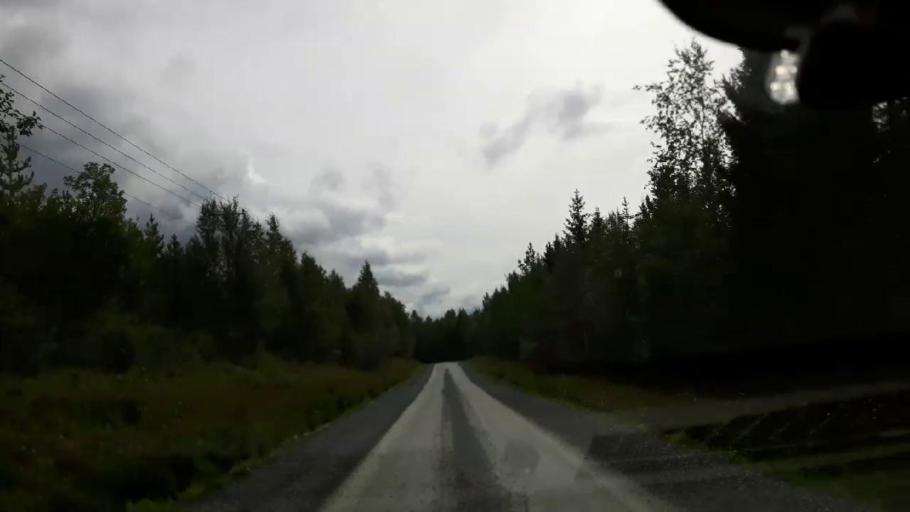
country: SE
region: Jaemtland
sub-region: Krokoms Kommun
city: Valla
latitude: 63.5922
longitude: 14.1426
